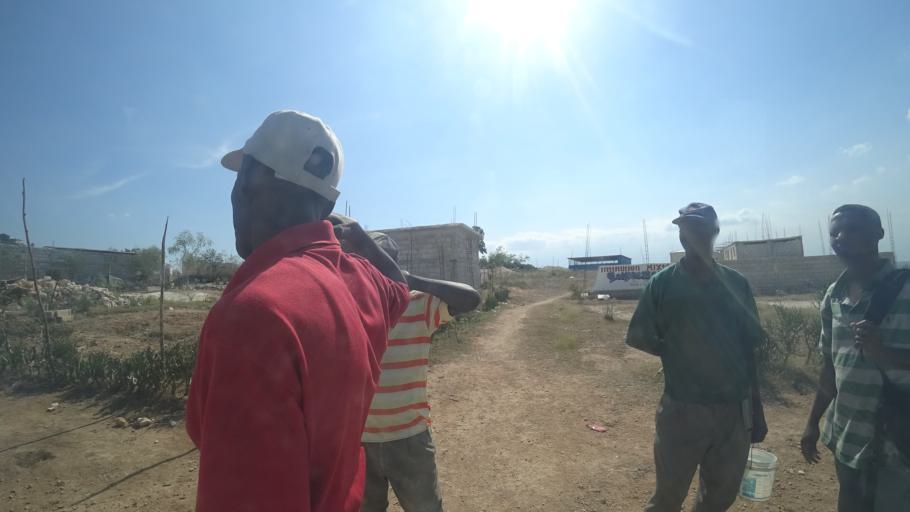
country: HT
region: Ouest
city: Croix des Bouquets
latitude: 18.6732
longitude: -72.2997
